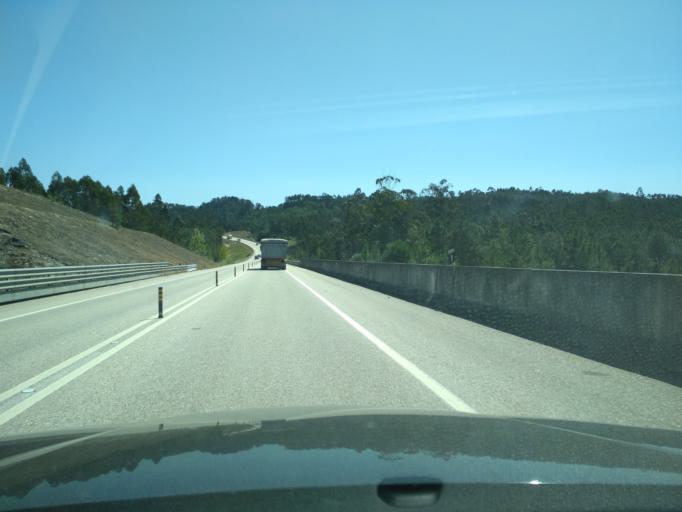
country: PT
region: Leiria
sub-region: Pombal
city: Lourical
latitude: 39.9615
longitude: -8.6936
